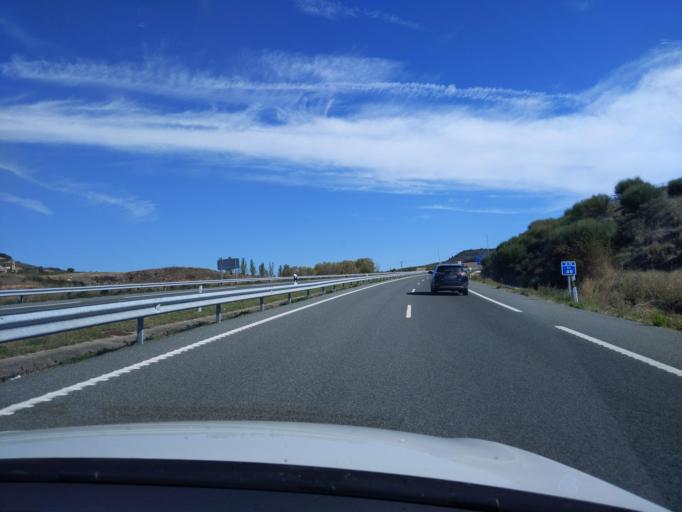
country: ES
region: Navarre
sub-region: Provincia de Navarra
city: Villamayor de Monjardin
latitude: 42.6170
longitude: -2.1081
